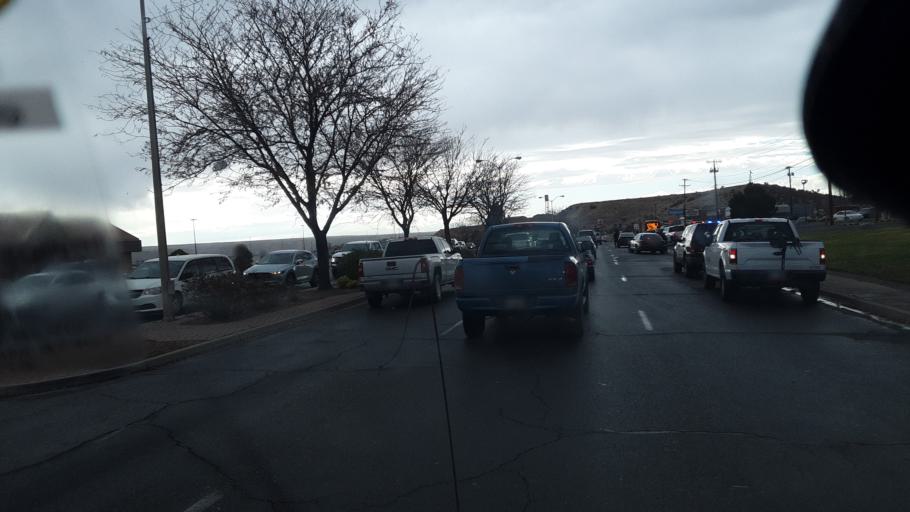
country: US
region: New Mexico
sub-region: San Juan County
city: Flora Vista
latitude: 36.7668
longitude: -108.1487
